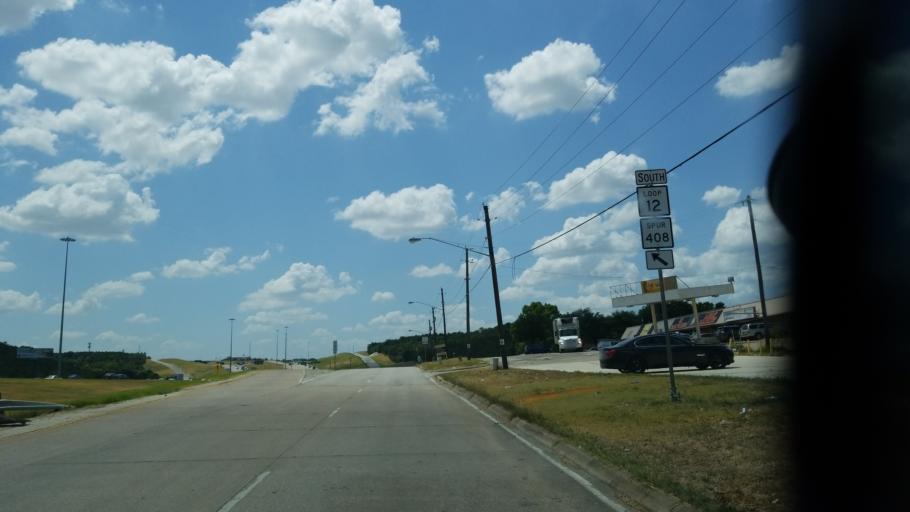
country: US
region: Texas
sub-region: Dallas County
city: Cockrell Hill
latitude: 32.7355
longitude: -96.9204
